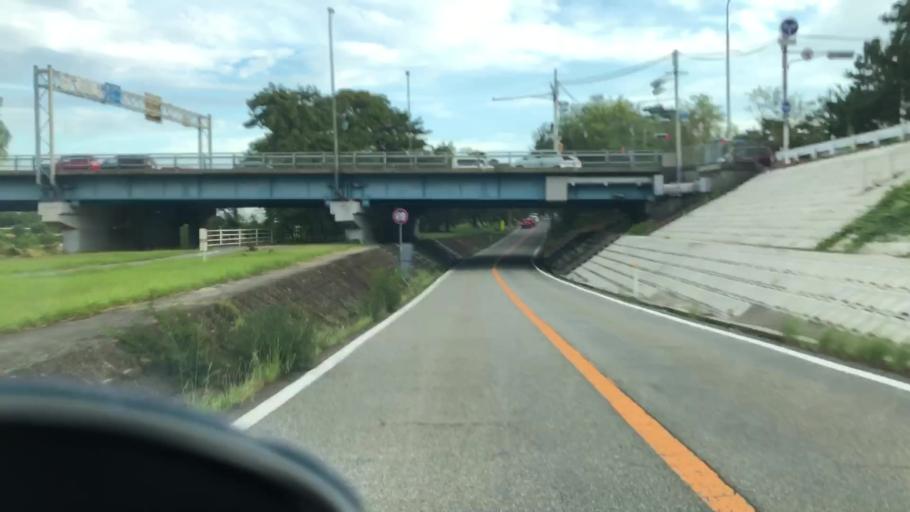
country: JP
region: Hyogo
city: Itami
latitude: 34.7652
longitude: 135.3724
